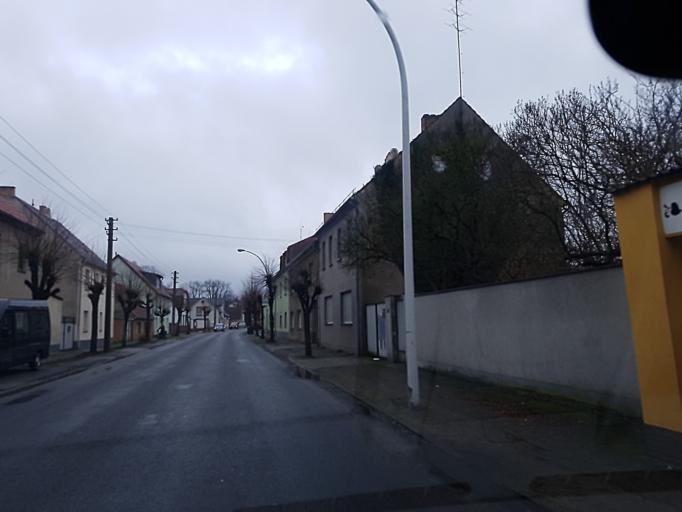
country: DE
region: Brandenburg
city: Finsterwalde
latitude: 51.6164
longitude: 13.7141
